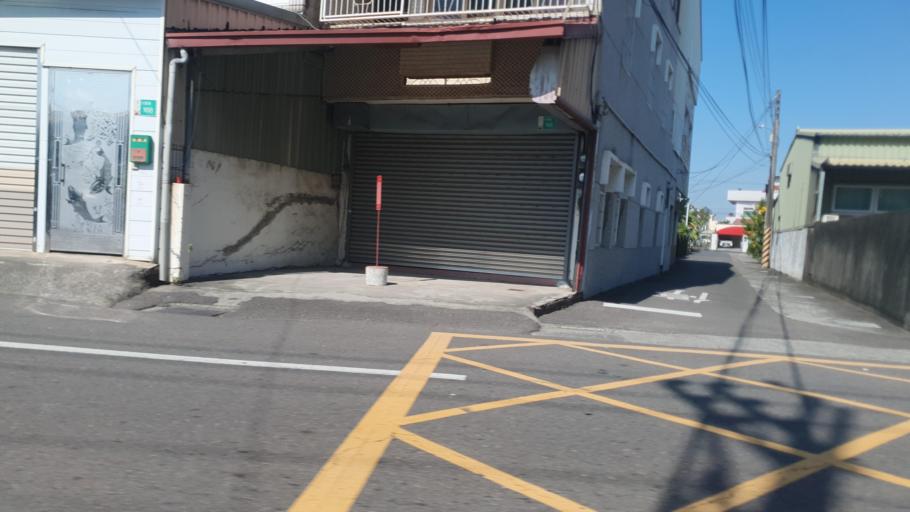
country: TW
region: Taiwan
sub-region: Tainan
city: Tainan
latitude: 23.0326
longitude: 120.2975
